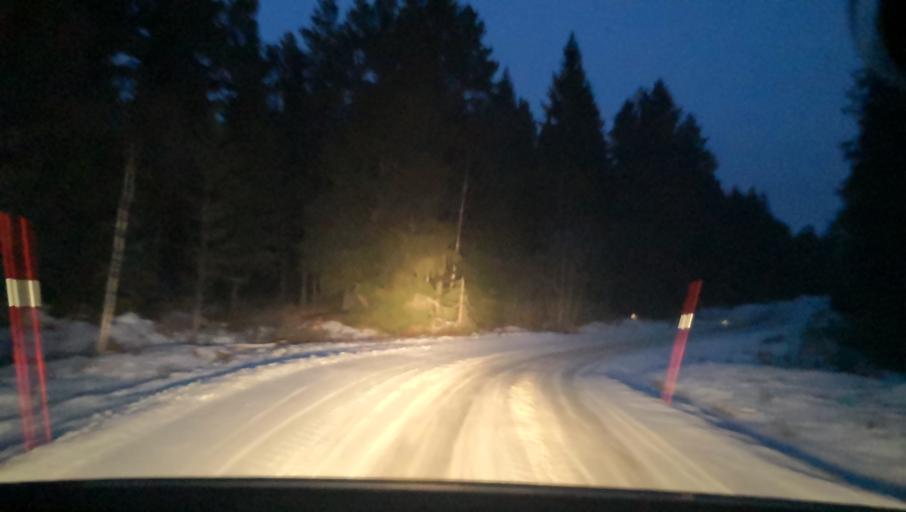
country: SE
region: Uppsala
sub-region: Heby Kommun
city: Tarnsjo
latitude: 60.2527
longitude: 16.7357
